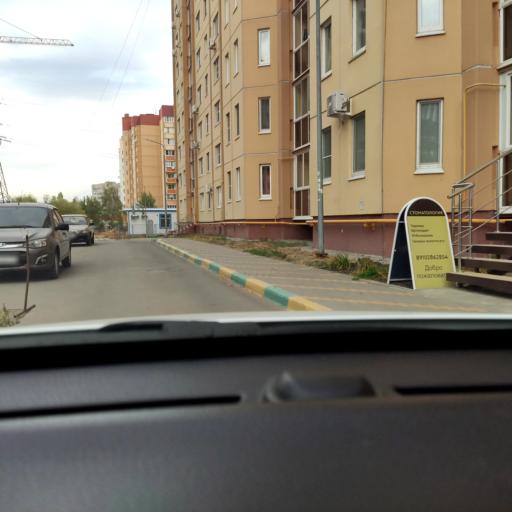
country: RU
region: Voronezj
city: Voronezh
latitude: 51.7175
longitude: 39.2629
